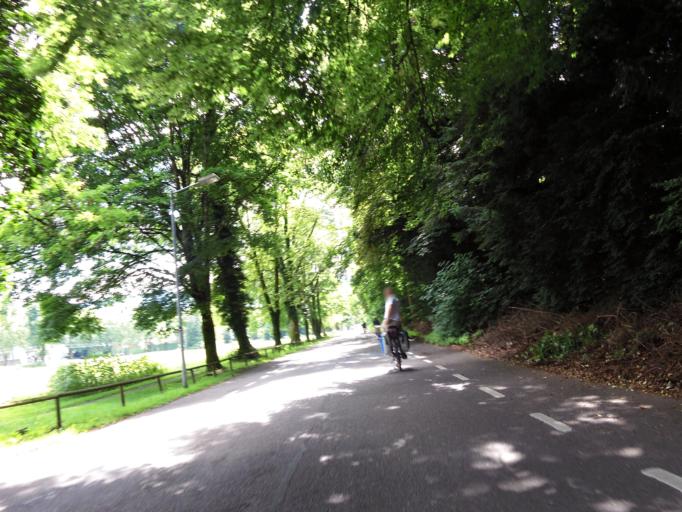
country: AT
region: Vorarlberg
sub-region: Politischer Bezirk Bregenz
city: Horbranz
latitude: 47.5445
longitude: 9.7239
